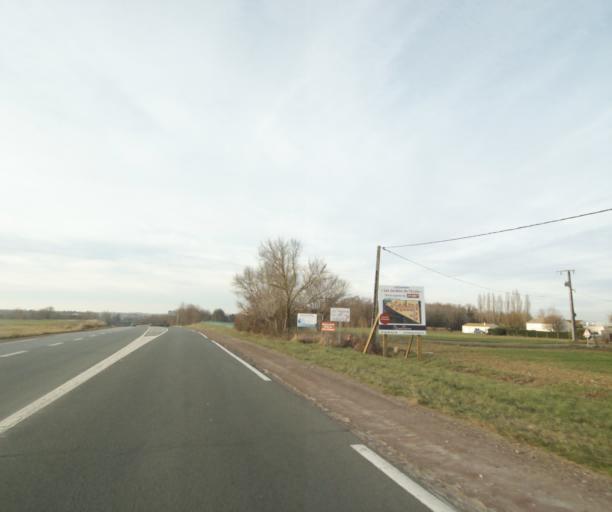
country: FR
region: Poitou-Charentes
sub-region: Departement de la Charente-Maritime
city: Saint-Porchaire
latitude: 45.8102
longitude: -0.7631
